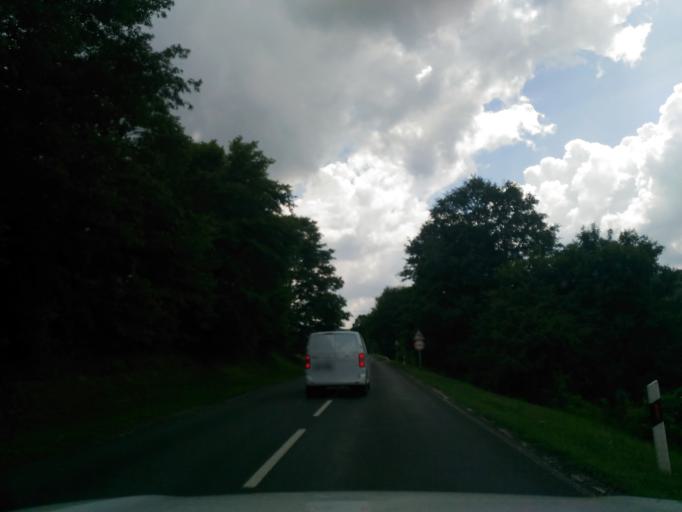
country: HU
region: Baranya
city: Komlo
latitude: 46.1736
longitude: 18.2115
